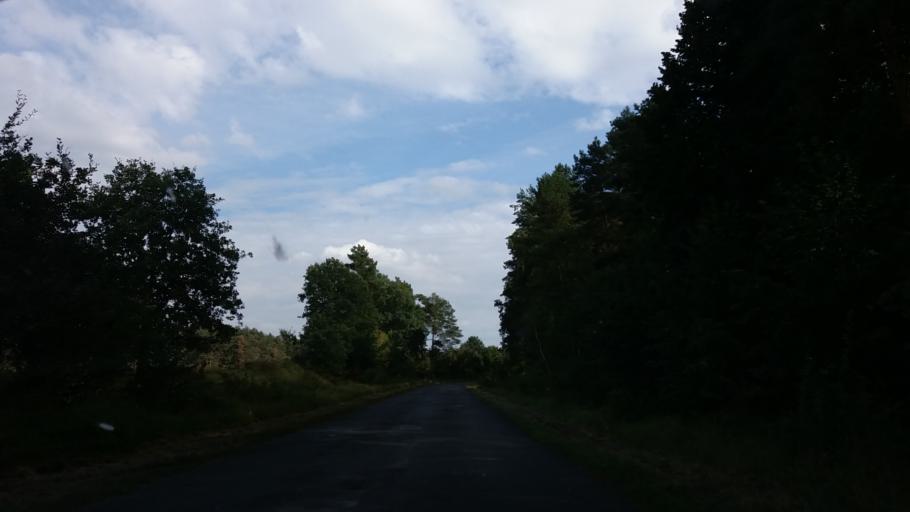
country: PL
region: West Pomeranian Voivodeship
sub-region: Powiat stargardzki
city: Dolice
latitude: 53.2393
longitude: 15.2450
